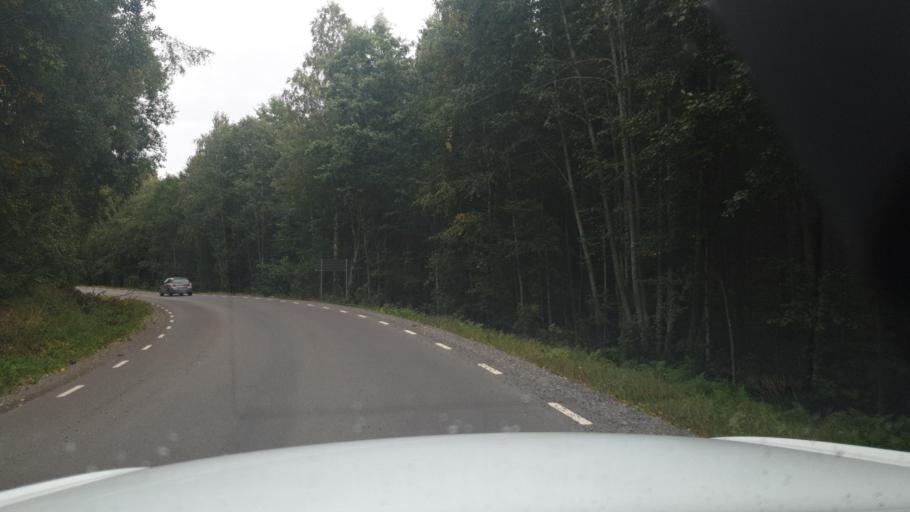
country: SE
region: Vaermland
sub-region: Torsby Kommun
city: Torsby
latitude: 59.9786
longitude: 12.8103
